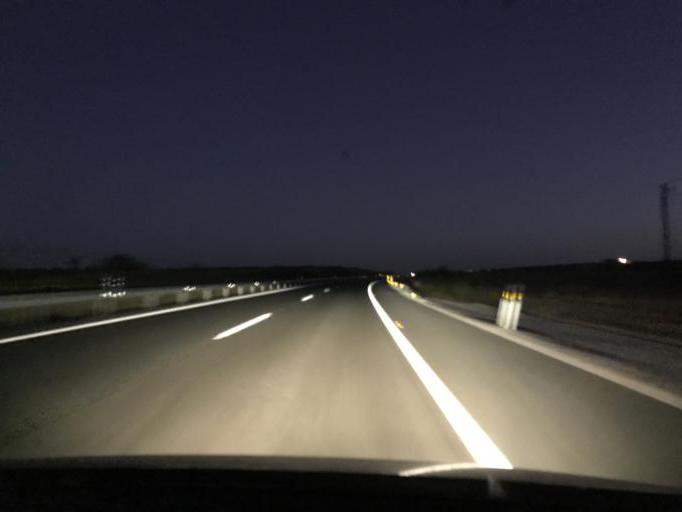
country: ES
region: Andalusia
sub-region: Provincia de Malaga
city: Antequera
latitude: 37.0920
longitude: -4.5497
